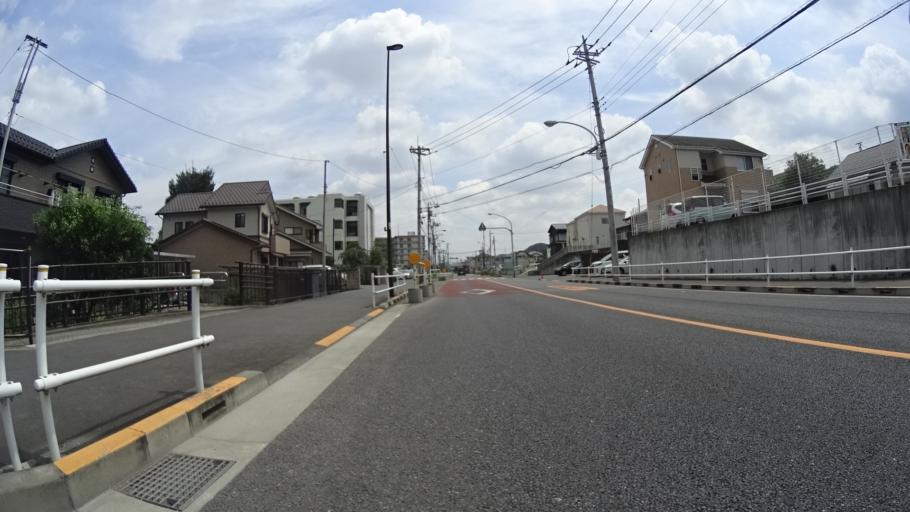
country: JP
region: Tokyo
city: Ome
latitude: 35.7816
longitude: 139.2672
